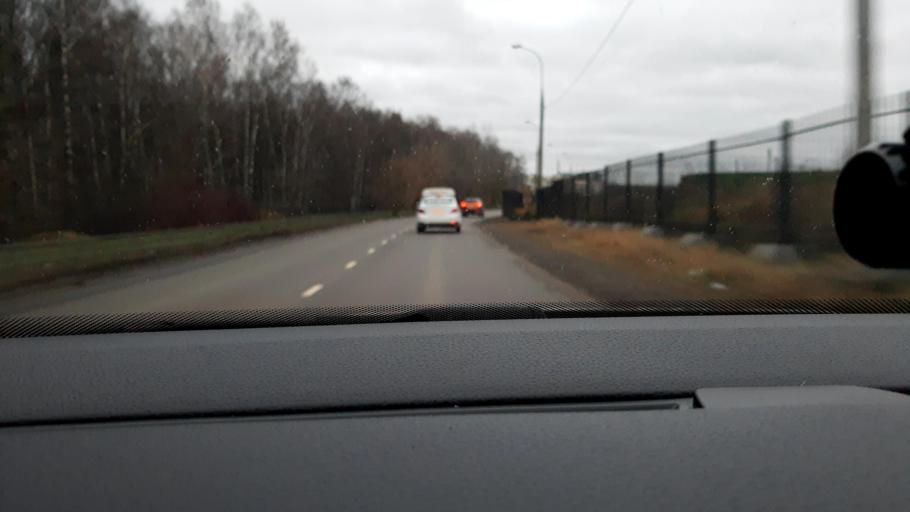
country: RU
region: Moskovskaya
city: Zarech'ye
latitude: 55.6815
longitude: 37.3995
